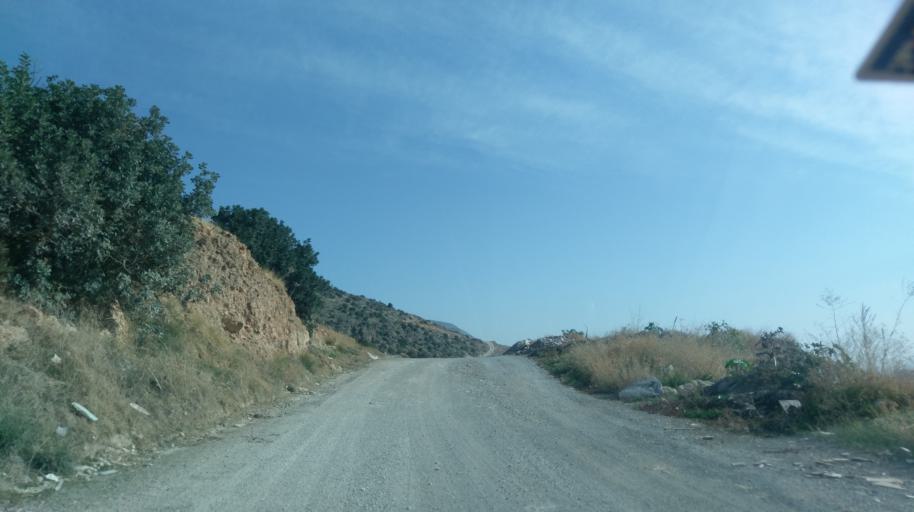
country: CY
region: Lefkosia
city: Nicosia
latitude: 35.2692
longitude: 33.4438
